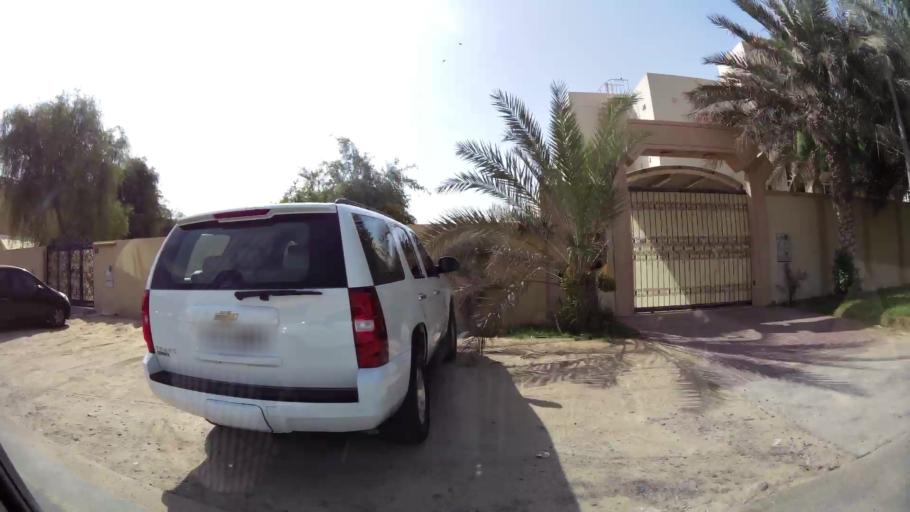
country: AE
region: Ash Shariqah
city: Sharjah
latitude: 25.2666
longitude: 55.3946
